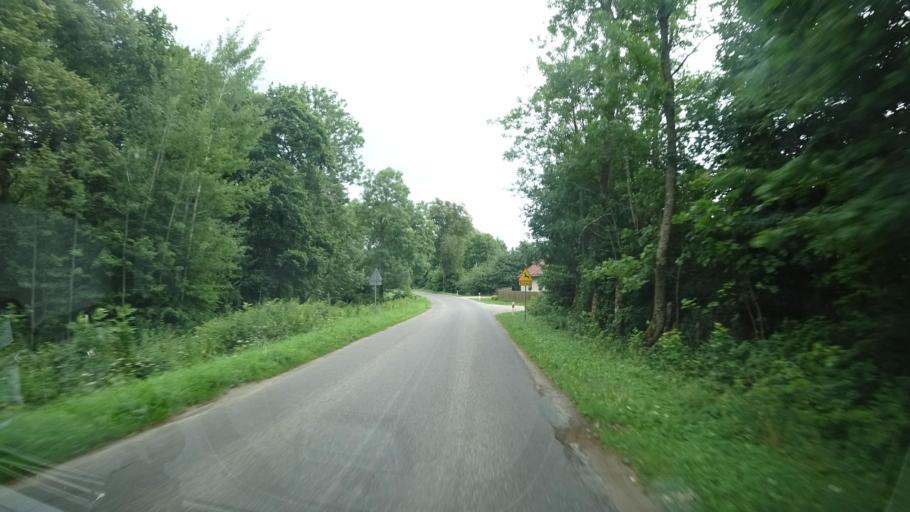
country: PL
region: Warmian-Masurian Voivodeship
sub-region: Powiat goldapski
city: Goldap
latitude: 54.3108
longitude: 22.3725
